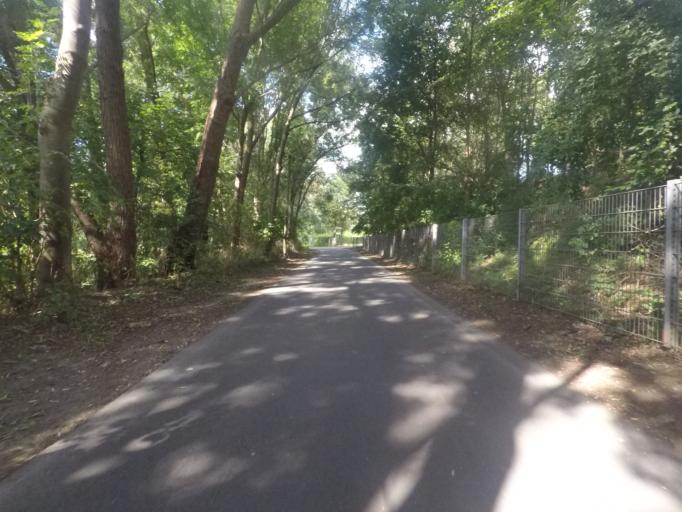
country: DE
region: North Rhine-Westphalia
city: Bad Oeynhausen
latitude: 52.2125
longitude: 8.8098
